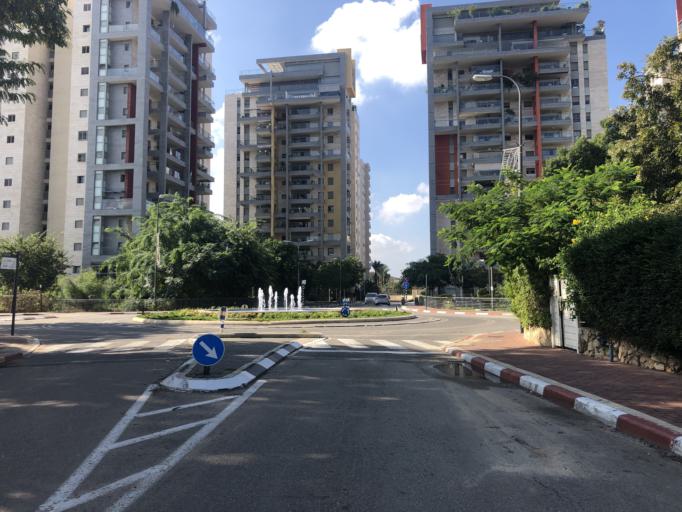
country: IL
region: Central District
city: Yehud
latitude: 32.0260
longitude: 34.8754
